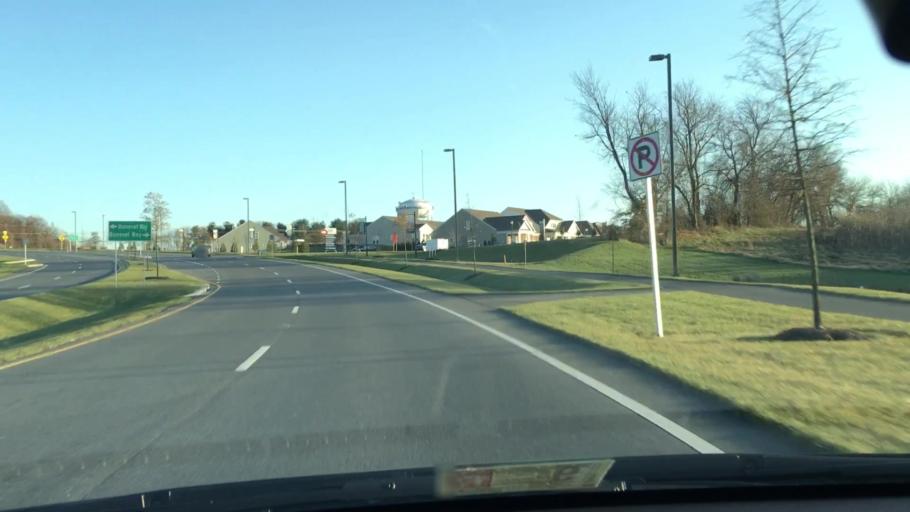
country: US
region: Maryland
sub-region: Montgomery County
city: Clarksburg
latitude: 39.2172
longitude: -77.2424
